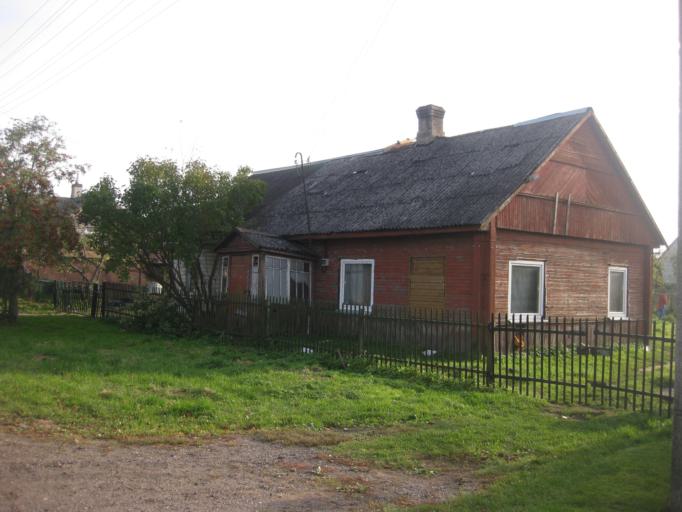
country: LT
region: Kauno apskritis
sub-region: Kaunas
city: Aleksotas
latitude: 54.8911
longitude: 23.8721
